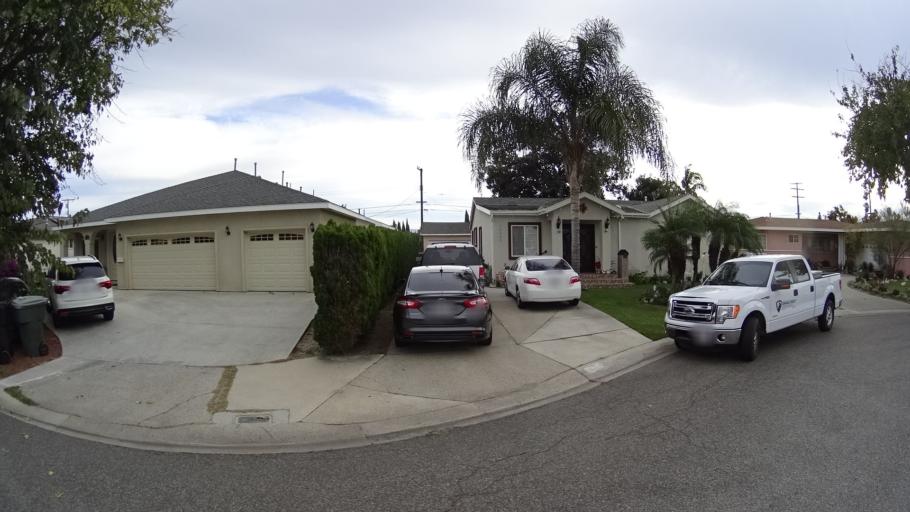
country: US
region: California
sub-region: Orange County
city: Garden Grove
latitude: 33.7753
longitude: -117.9263
